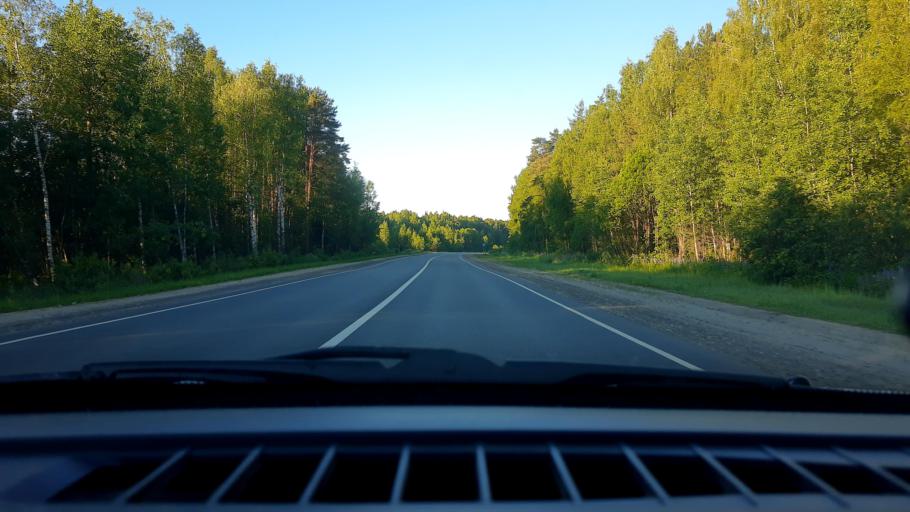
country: RU
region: Nizjnij Novgorod
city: Linda
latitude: 56.6477
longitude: 44.1145
